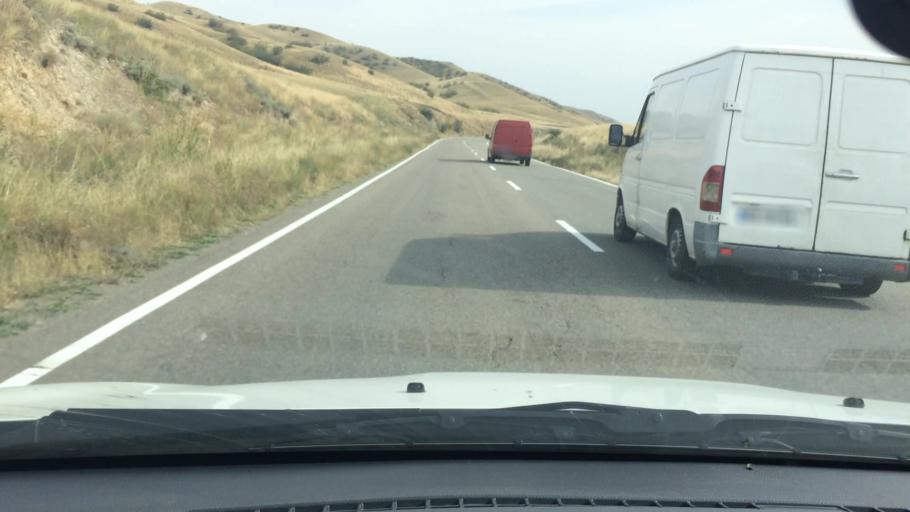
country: GE
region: Kvemo Kartli
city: Rust'avi
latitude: 41.4991
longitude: 44.9585
